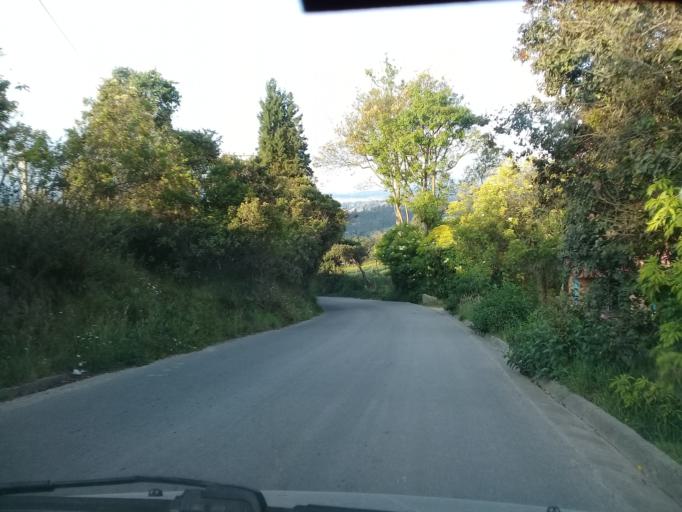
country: CO
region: Cundinamarca
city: Sibate
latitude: 4.4576
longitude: -74.2680
